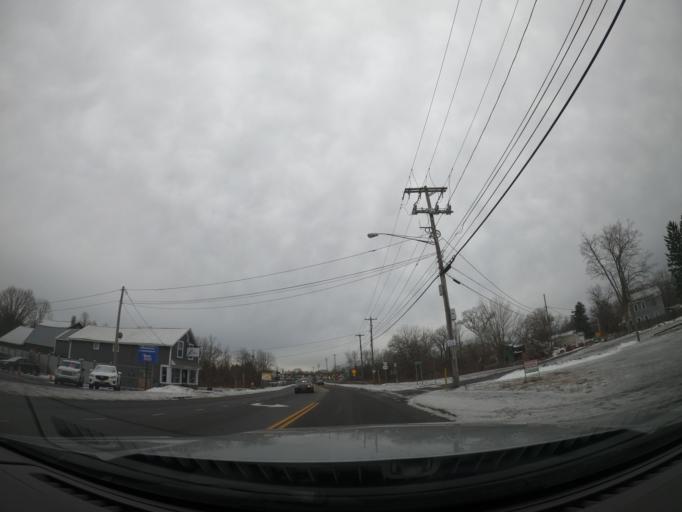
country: US
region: New York
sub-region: Madison County
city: Bridgeport
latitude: 43.1554
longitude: -75.9702
